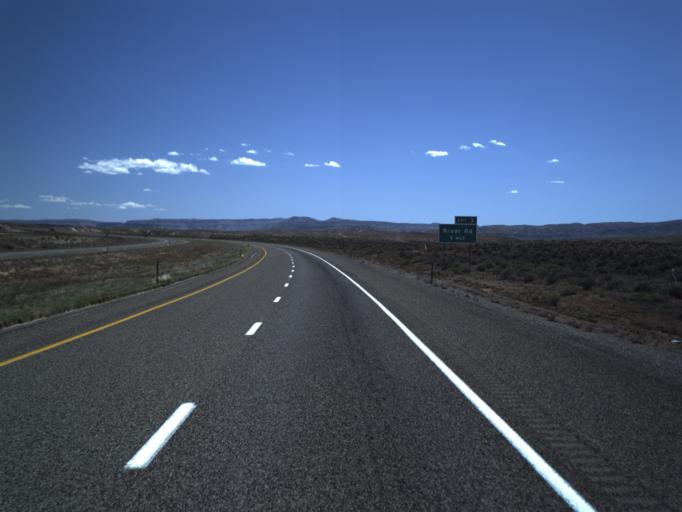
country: US
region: Utah
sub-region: Washington County
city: Saint George
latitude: 37.0034
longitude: -113.5820
